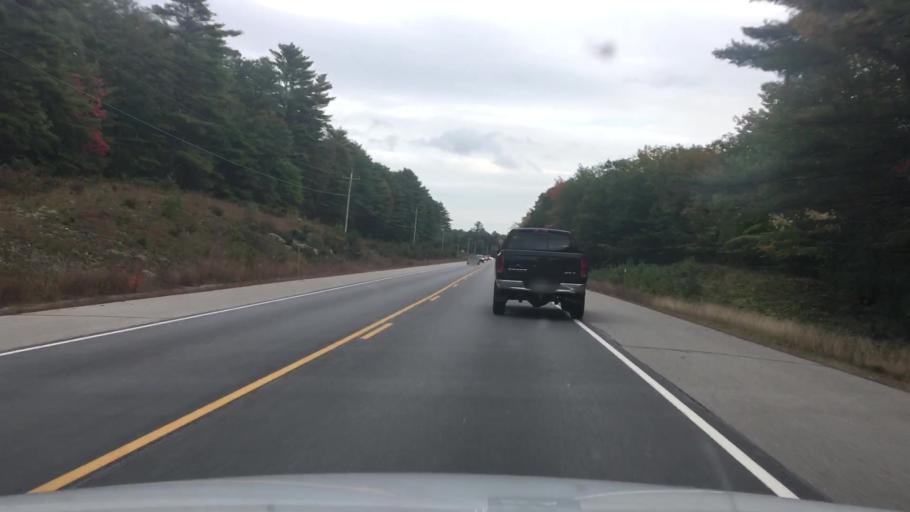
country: US
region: New Hampshire
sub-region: Strafford County
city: New Durham
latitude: 43.4345
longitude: -71.1815
